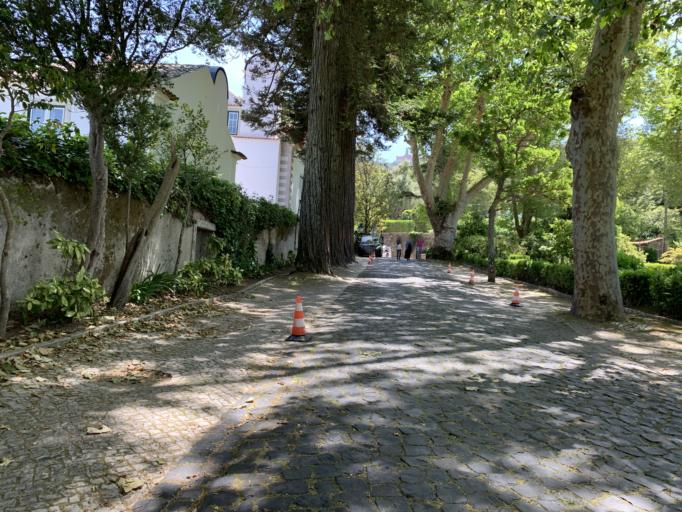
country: PT
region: Lisbon
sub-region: Sintra
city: Sintra
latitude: 38.7965
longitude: -9.3987
